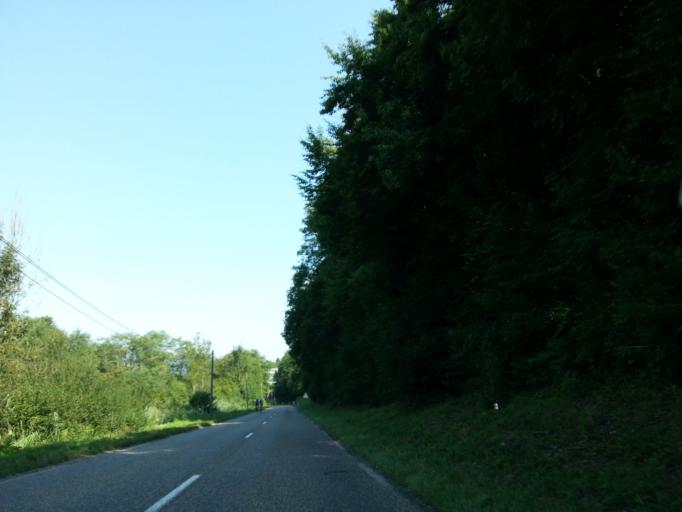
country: FR
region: Rhone-Alpes
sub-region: Departement de la Haute-Savoie
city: Doussard
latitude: 45.7958
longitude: 6.2318
